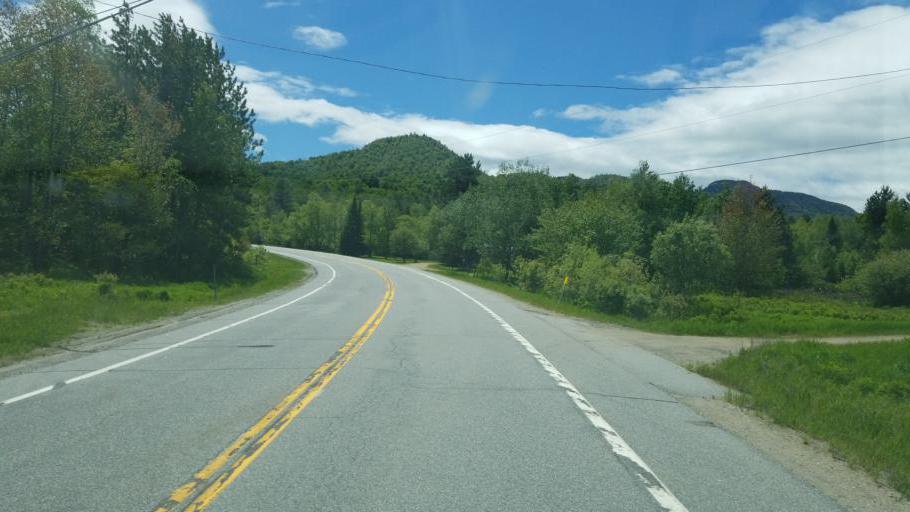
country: US
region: New York
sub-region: Hamilton County
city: Lake Pleasant
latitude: 43.7103
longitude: -74.3301
